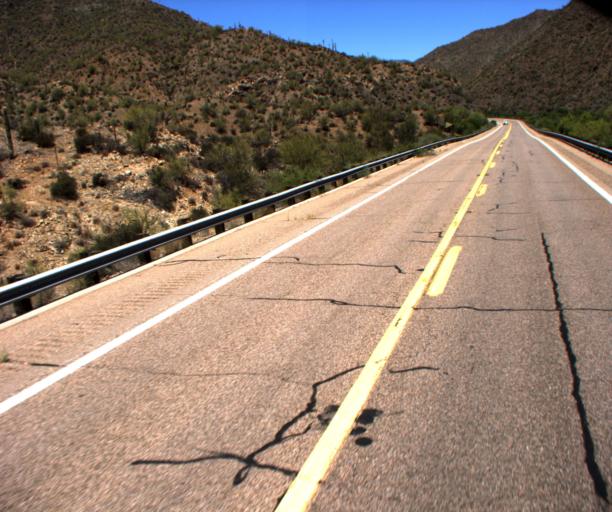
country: US
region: Arizona
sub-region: Pinal County
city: Kearny
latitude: 33.0480
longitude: -110.7176
